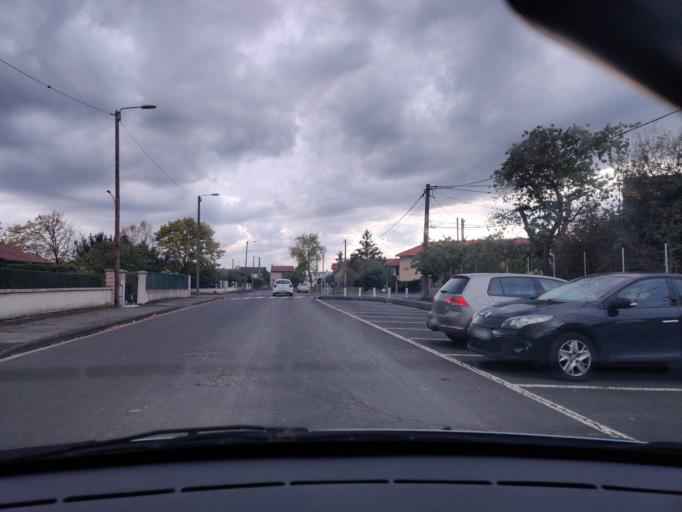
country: FR
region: Auvergne
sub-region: Departement du Puy-de-Dome
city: Menetrol
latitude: 45.8830
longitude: 3.1274
